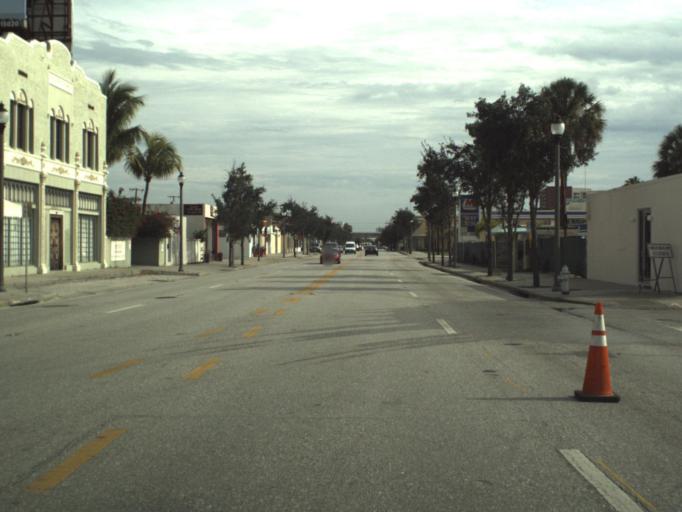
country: US
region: Florida
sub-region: Palm Beach County
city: West Palm Beach
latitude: 26.7198
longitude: -80.0533
